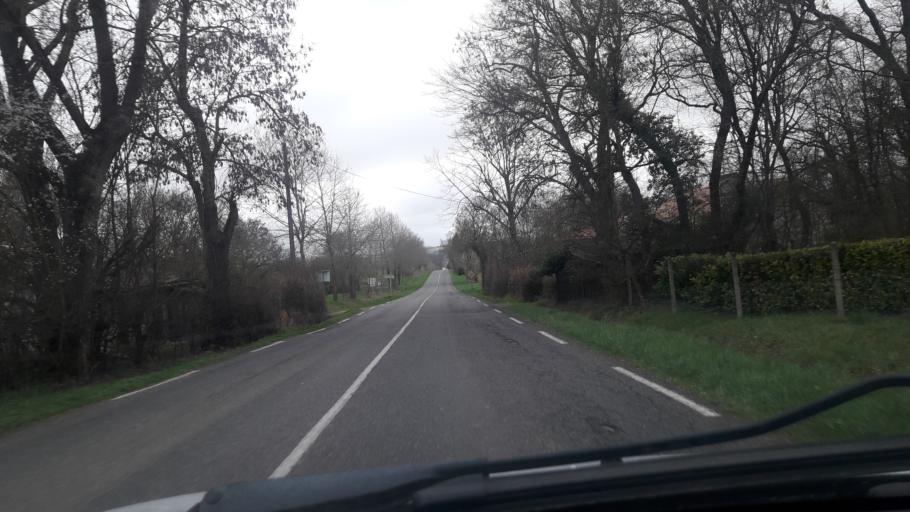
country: FR
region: Midi-Pyrenees
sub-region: Departement du Gers
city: Gimont
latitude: 43.6645
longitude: 1.0192
